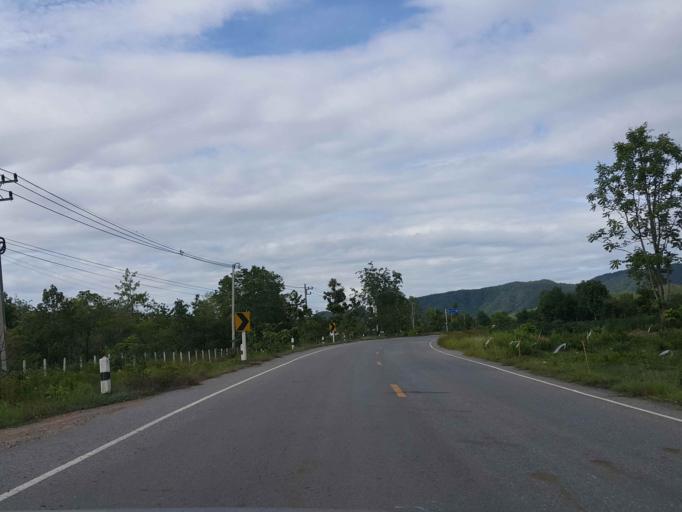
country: TH
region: Sukhothai
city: Thung Saliam
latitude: 17.2361
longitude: 99.5152
